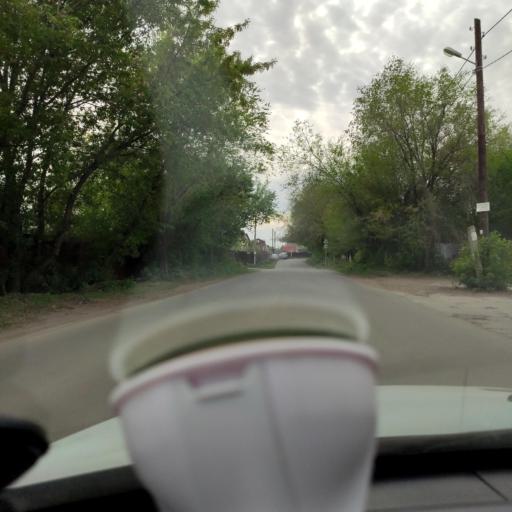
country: RU
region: Samara
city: Smyshlyayevka
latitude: 53.2082
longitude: 50.3277
